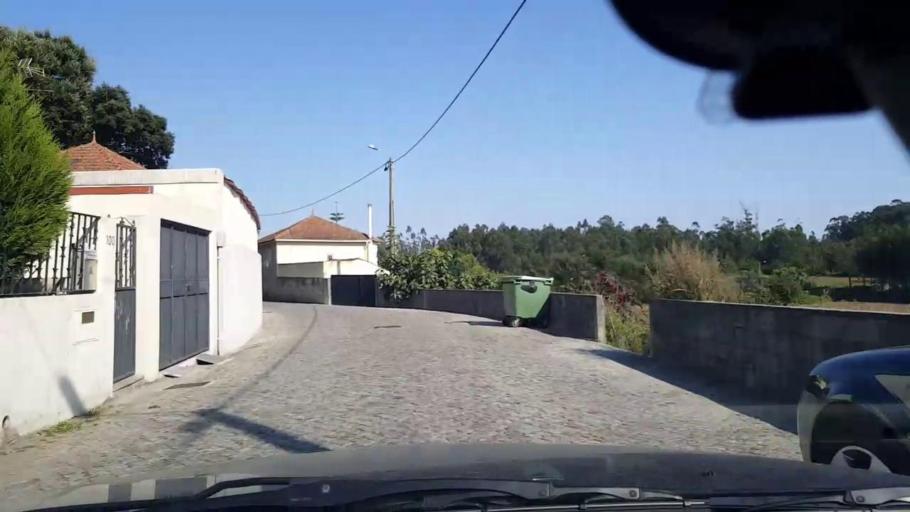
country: PT
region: Porto
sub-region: Vila do Conde
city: Arvore
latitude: 41.3574
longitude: -8.7042
